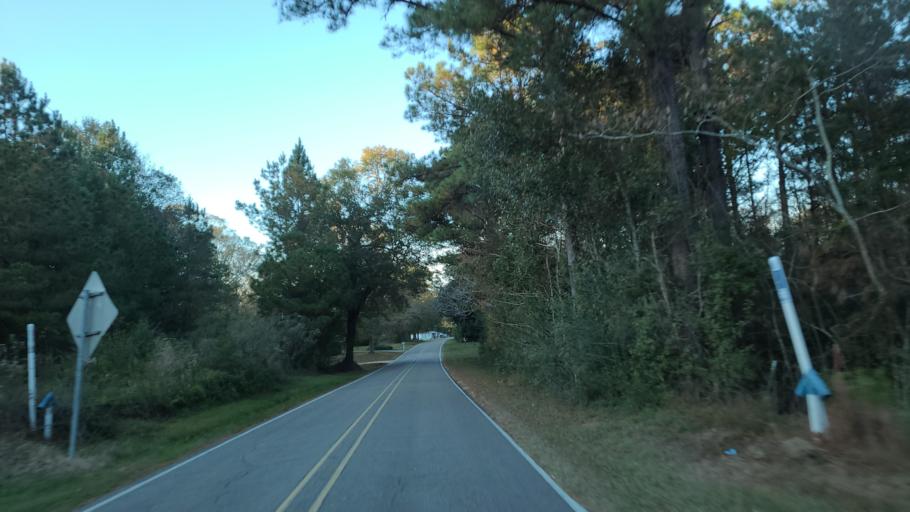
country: US
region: Mississippi
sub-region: Stone County
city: Wiggins
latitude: 30.9888
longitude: -89.2593
